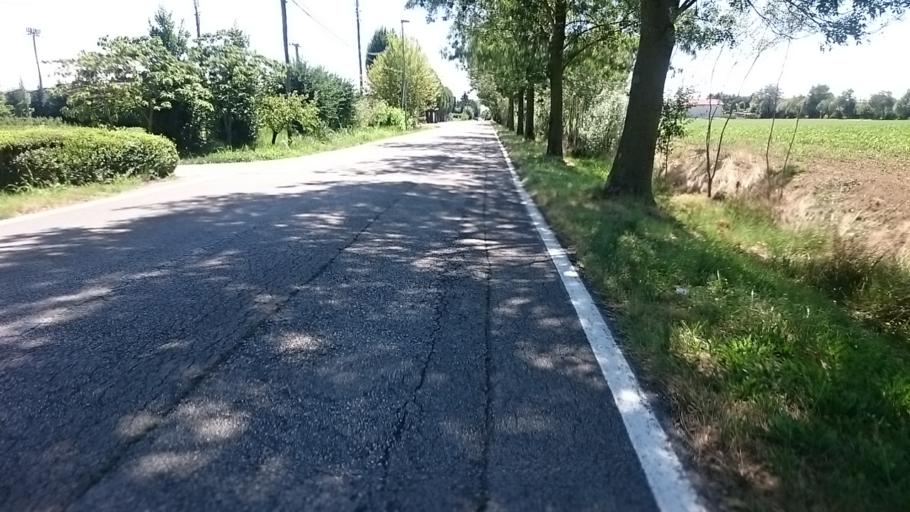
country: IT
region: Veneto
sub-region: Provincia di Padova
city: Villanova
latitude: 45.4858
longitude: 11.9760
